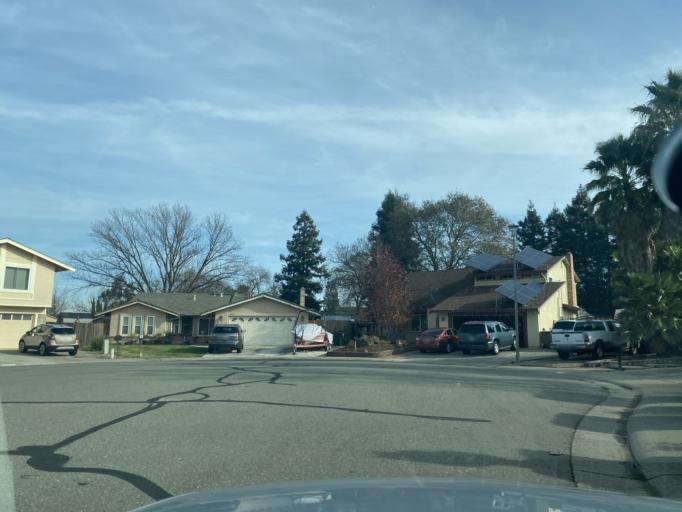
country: US
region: California
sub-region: Sacramento County
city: Elk Grove
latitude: 38.3991
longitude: -121.3800
